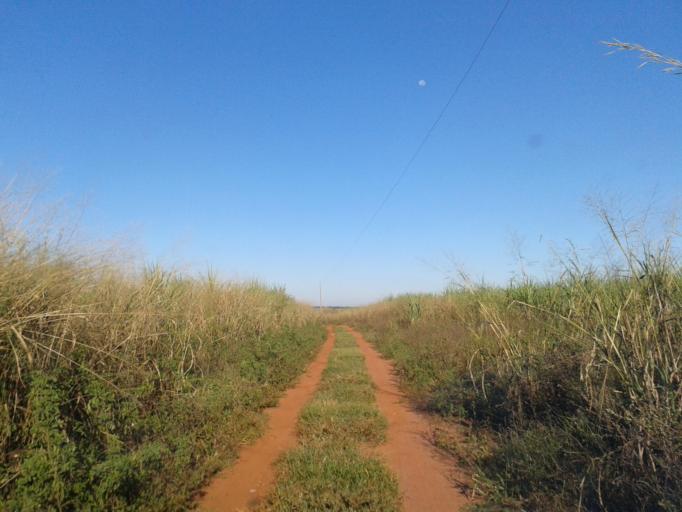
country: BR
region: Minas Gerais
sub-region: Santa Vitoria
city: Santa Vitoria
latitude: -19.0204
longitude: -50.3603
